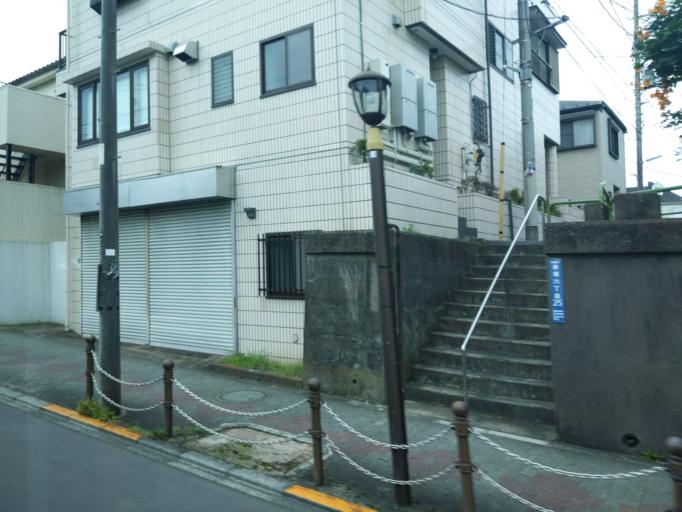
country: JP
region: Saitama
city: Wako
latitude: 35.7772
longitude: 139.6470
